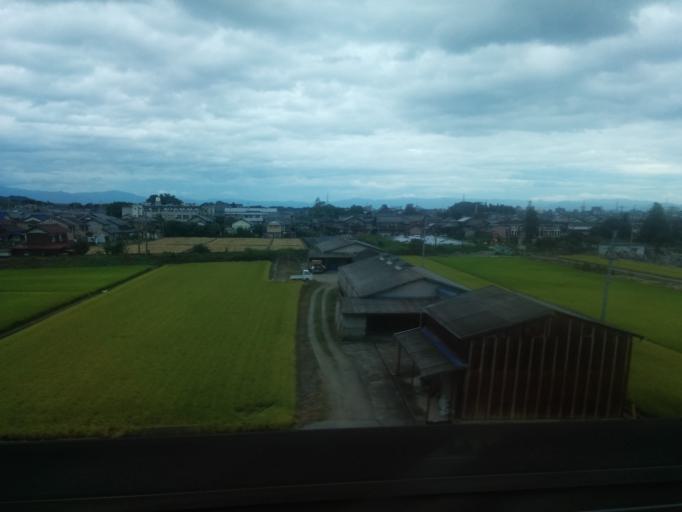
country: JP
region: Shiga Prefecture
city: Hikone
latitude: 35.2304
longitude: 136.2616
